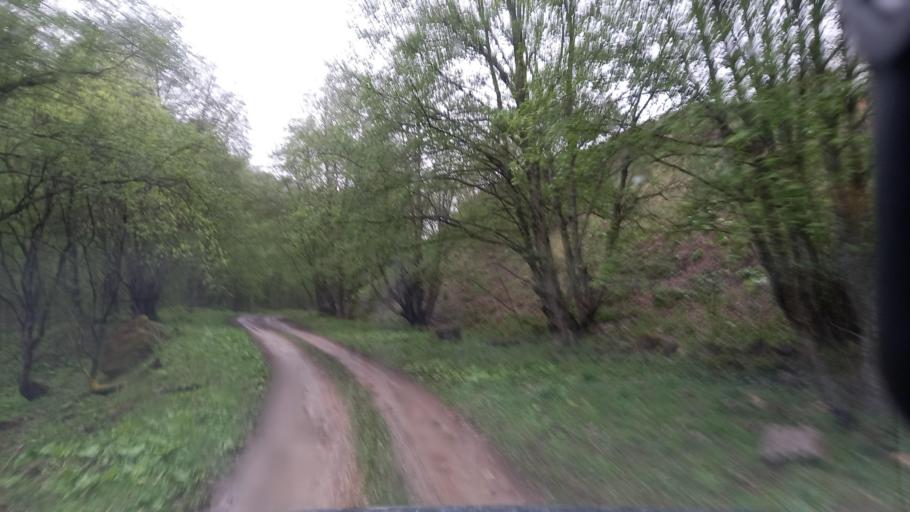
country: RU
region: Kabardino-Balkariya
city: Bylym
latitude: 43.5944
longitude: 42.9668
